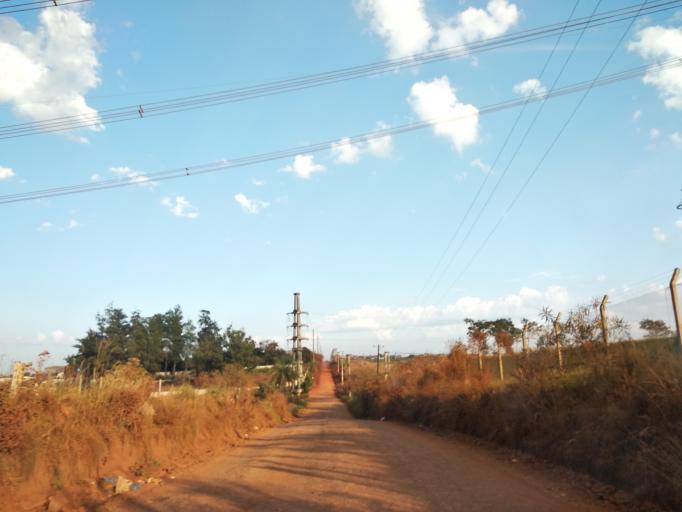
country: AR
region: Misiones
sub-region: Departamento de Capital
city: Posadas
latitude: -27.4448
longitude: -55.9185
